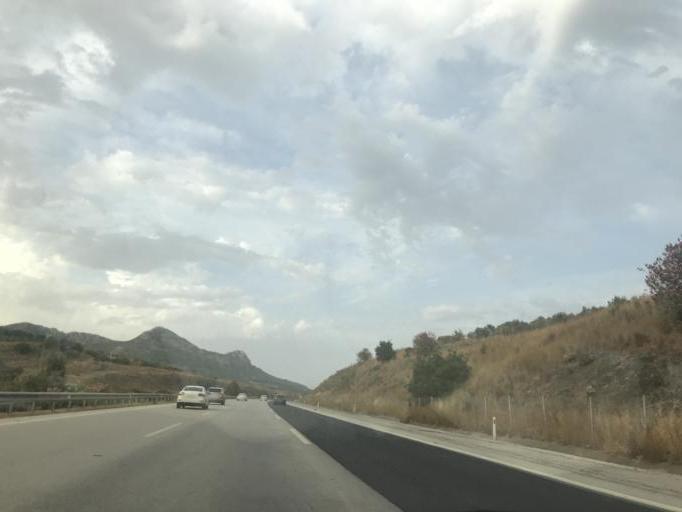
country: TR
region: Adana
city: Ceyhan
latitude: 37.0116
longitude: 35.9649
